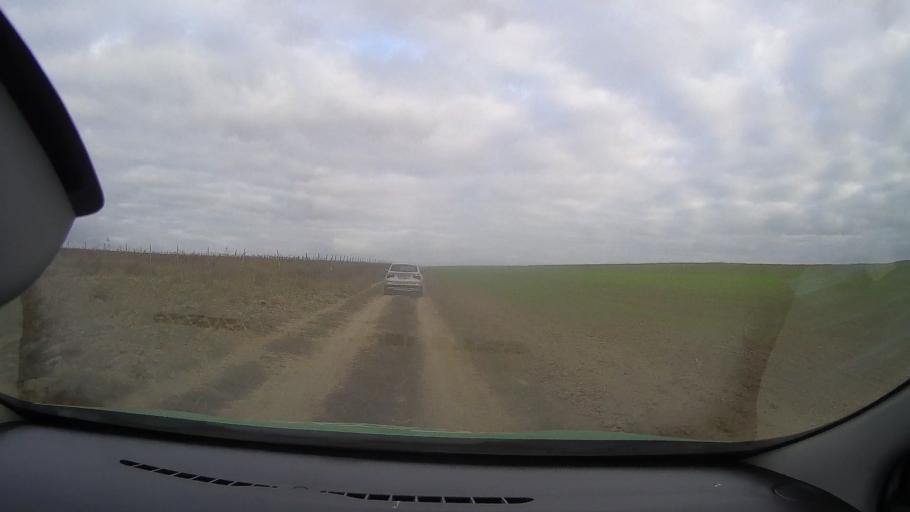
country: RO
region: Tulcea
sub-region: Comuna Jurilovca
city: Jurilovca
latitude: 44.7650
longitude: 28.9070
